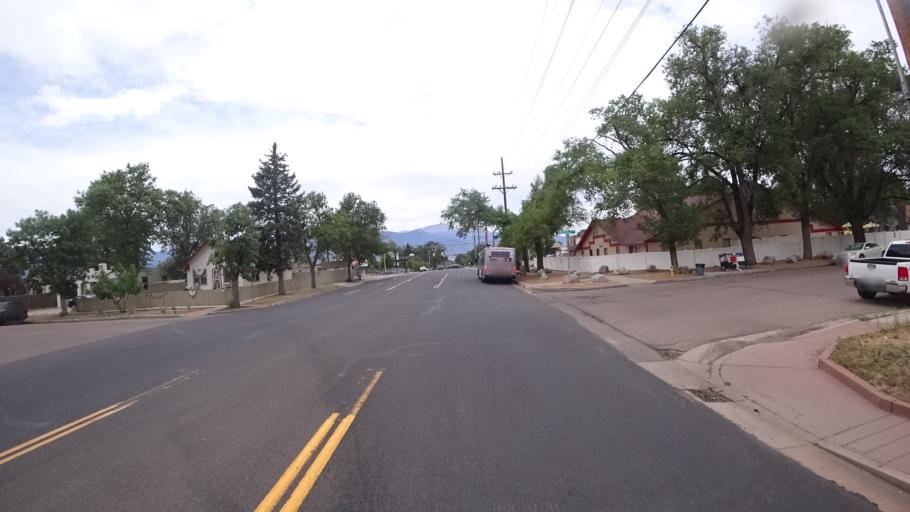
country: US
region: Colorado
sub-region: El Paso County
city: Colorado Springs
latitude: 38.8386
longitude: -104.7928
